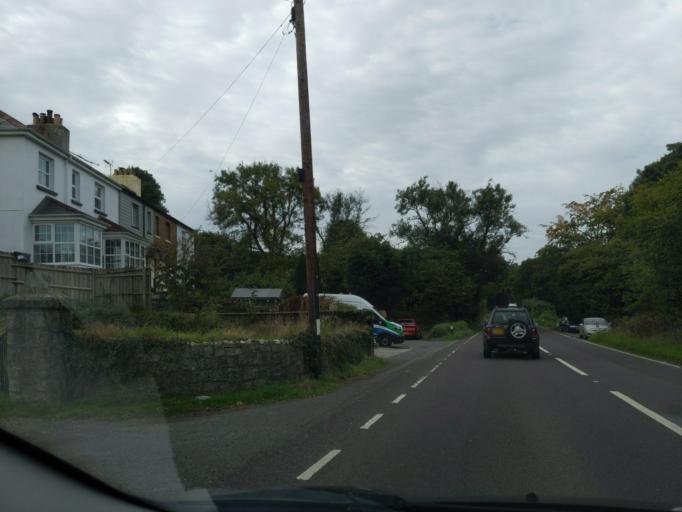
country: GB
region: England
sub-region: Cornwall
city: Wadebridge
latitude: 50.5078
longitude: -4.7949
